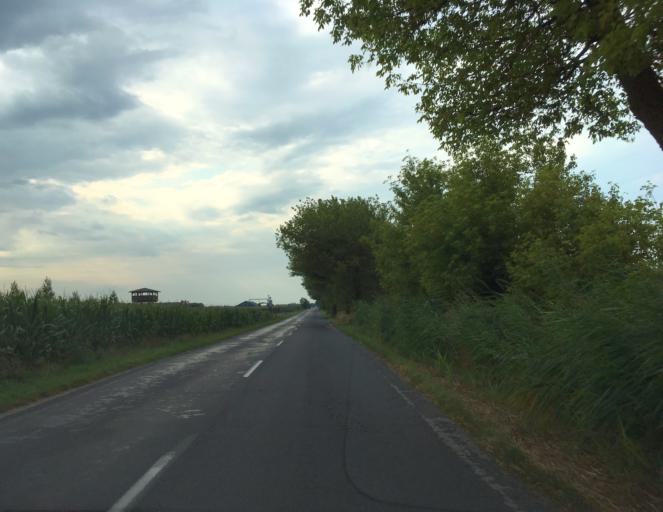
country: SK
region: Trnavsky
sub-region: Okres Dunajska Streda
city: Velky Meder
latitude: 47.9241
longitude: 17.7377
